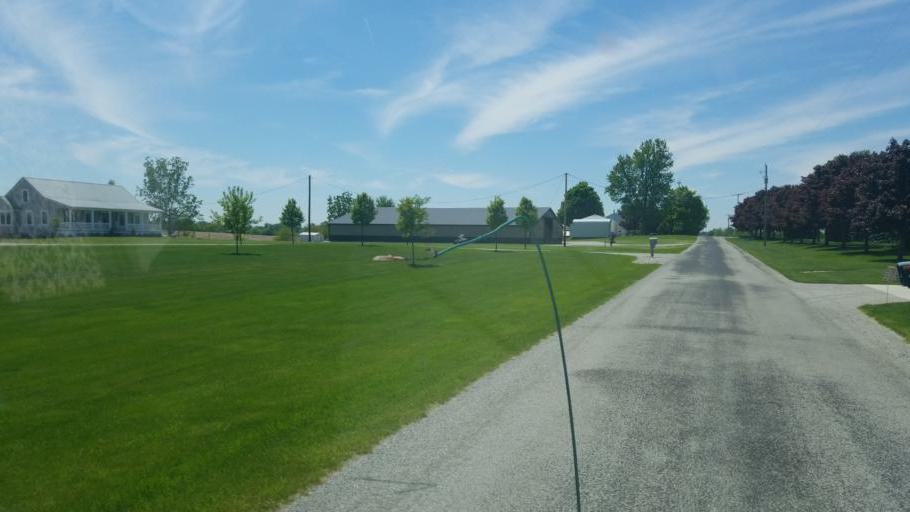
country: US
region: Ohio
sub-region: Huron County
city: Norwalk
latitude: 41.1193
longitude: -82.6019
